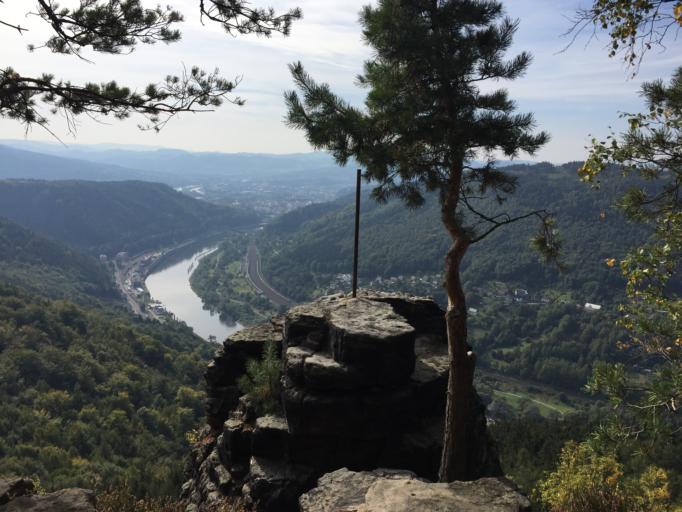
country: CZ
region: Ustecky
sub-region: Okres Decin
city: Decin
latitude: 50.8060
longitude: 14.2444
